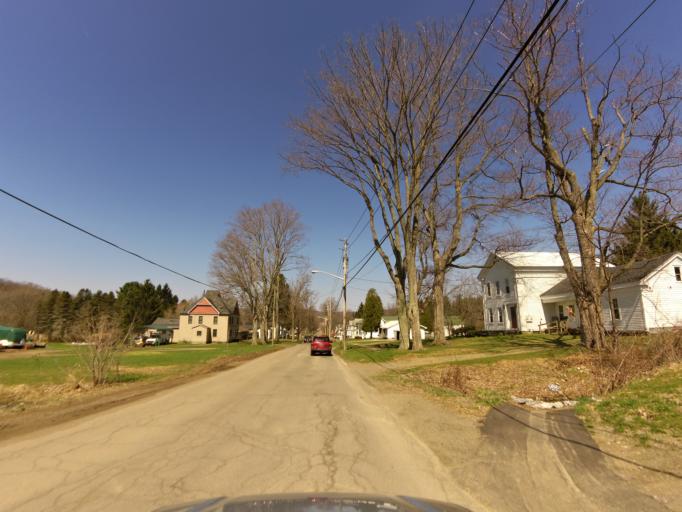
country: US
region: New York
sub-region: Cattaraugus County
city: Franklinville
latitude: 42.3336
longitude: -78.4465
